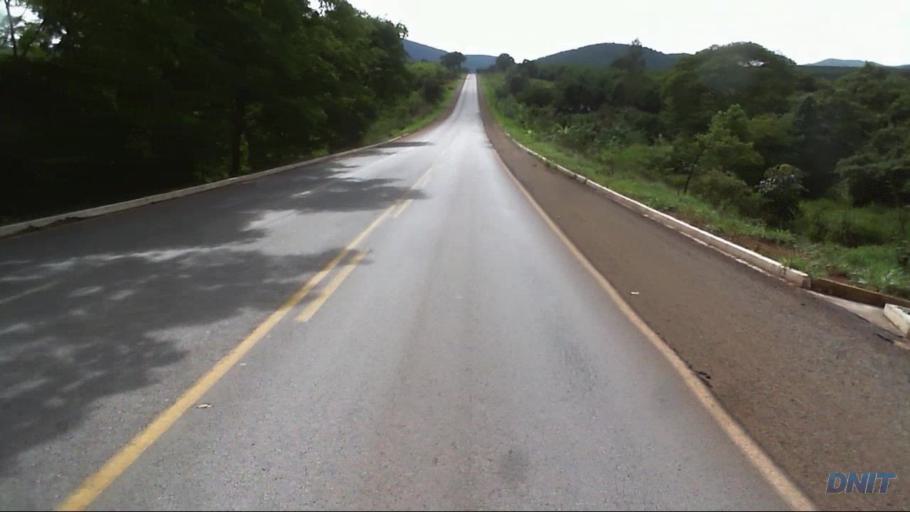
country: BR
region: Goias
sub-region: Barro Alto
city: Barro Alto
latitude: -14.8711
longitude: -49.0048
